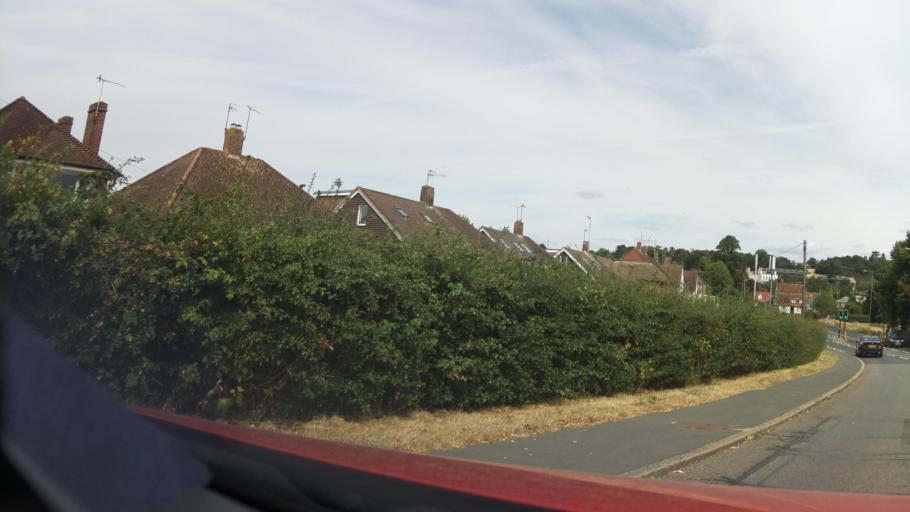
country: GB
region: England
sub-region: Surrey
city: Reigate
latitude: 51.2219
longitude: -0.1993
